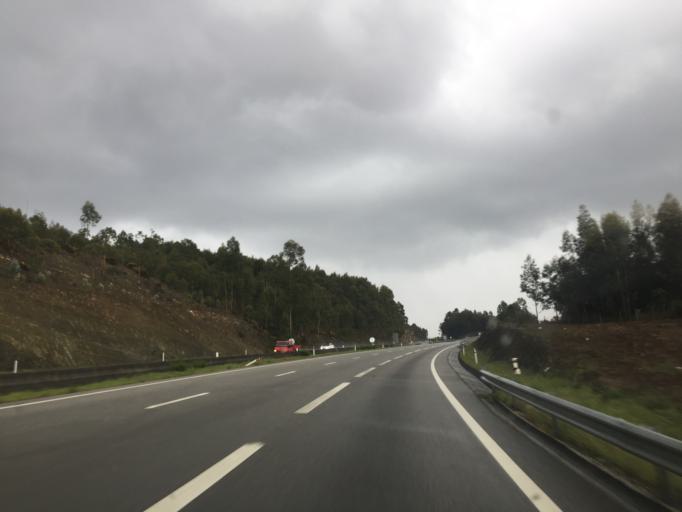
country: PT
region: Aveiro
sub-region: Agueda
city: Valongo
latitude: 40.6592
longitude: -8.3858
